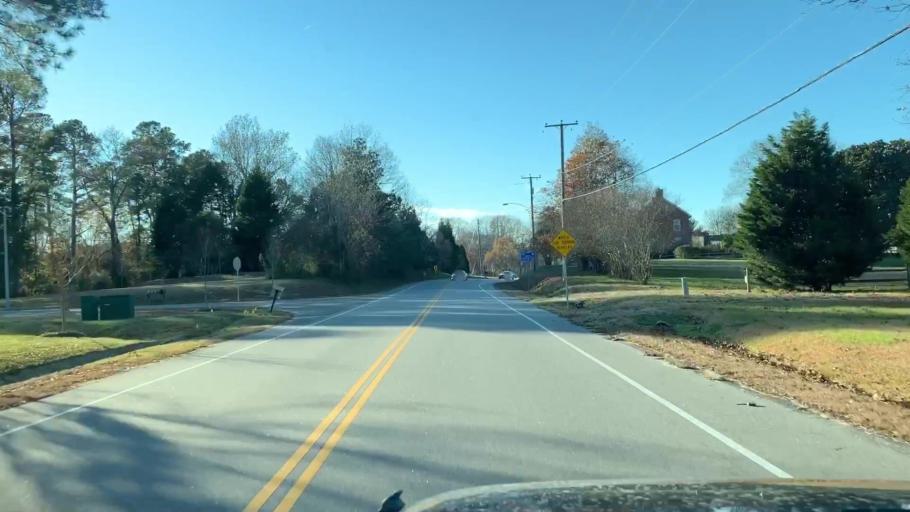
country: US
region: Virginia
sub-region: James City County
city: Williamsburg
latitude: 37.3820
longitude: -76.8077
